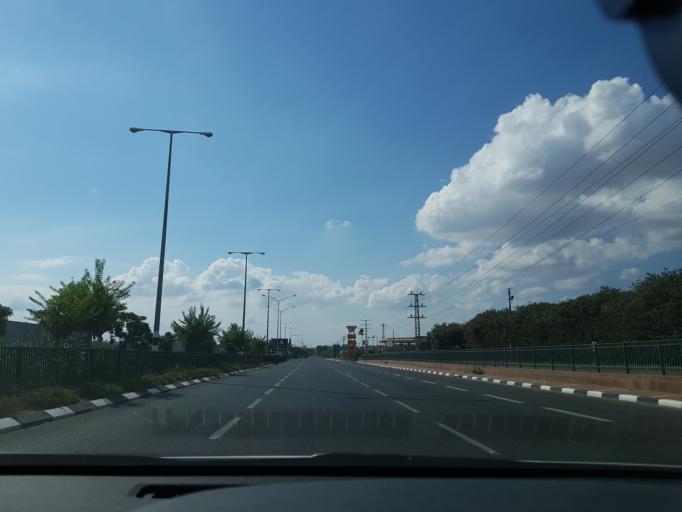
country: IL
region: Central District
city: Ness Ziona
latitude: 31.9470
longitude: 34.8013
